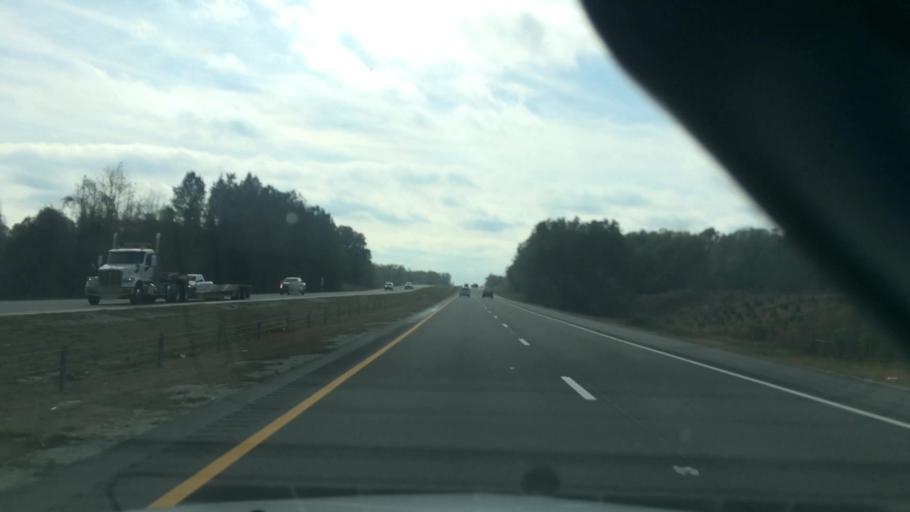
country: US
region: North Carolina
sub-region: New Hanover County
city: Wrightsboro
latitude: 34.3134
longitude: -77.9472
